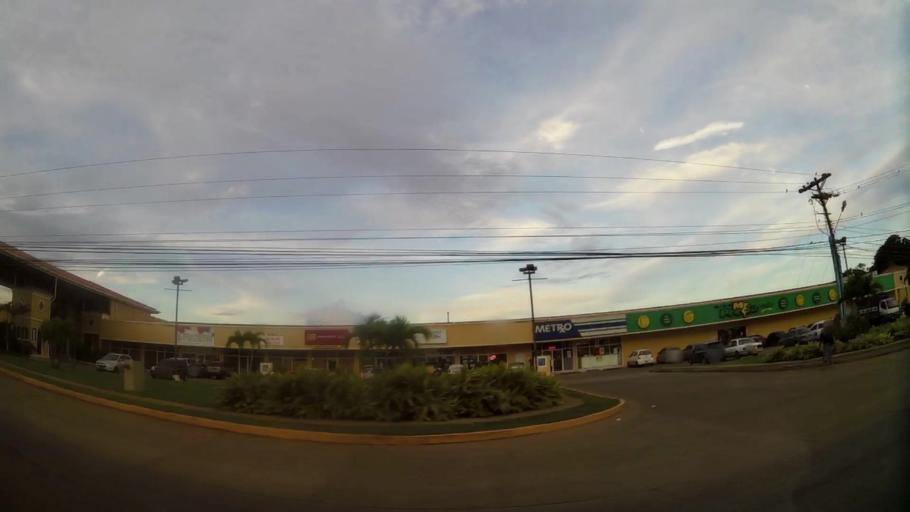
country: PA
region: Panama
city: La Chorrera
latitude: 8.8660
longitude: -79.7650
